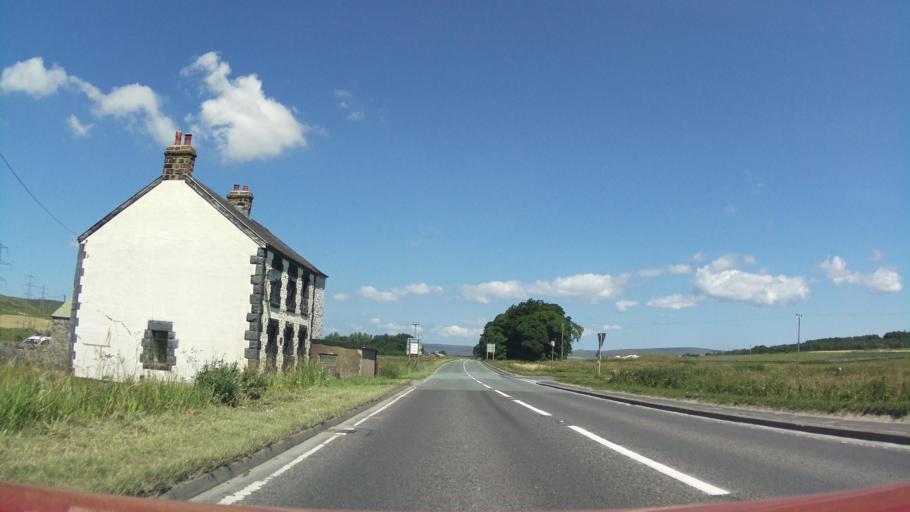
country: GB
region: England
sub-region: Derbyshire
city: Buxton
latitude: 53.2817
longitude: -1.8904
